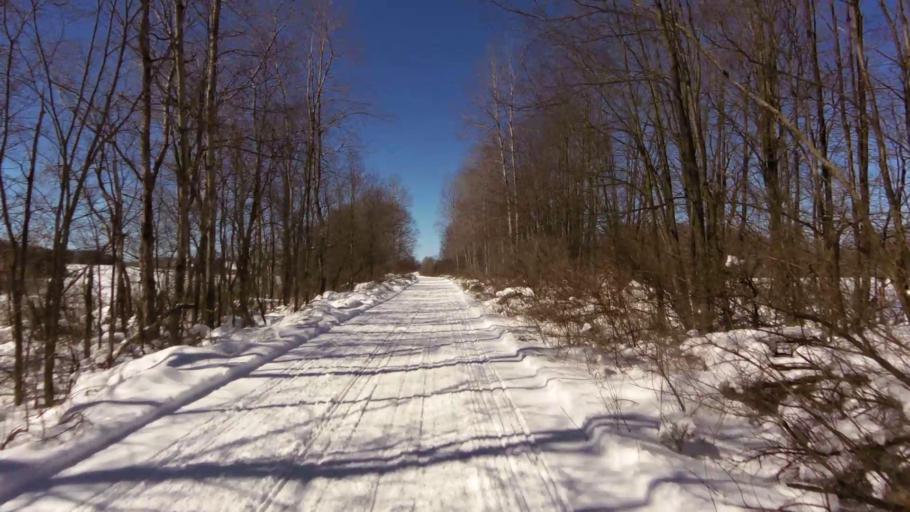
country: US
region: New York
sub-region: Cattaraugus County
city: Delevan
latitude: 42.4379
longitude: -78.4144
